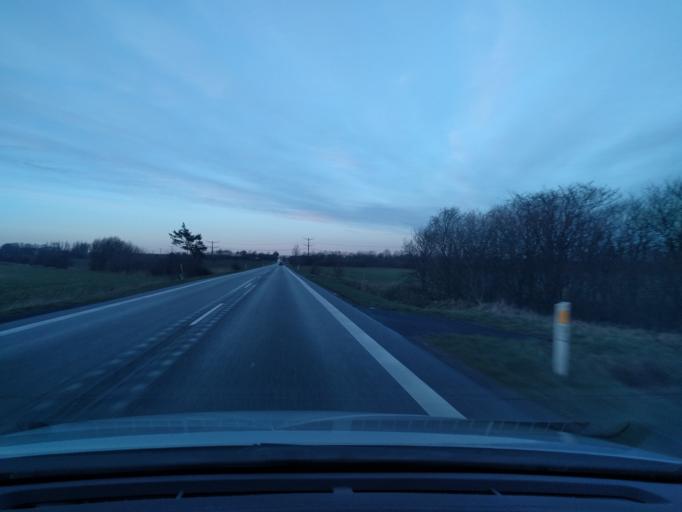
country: DK
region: South Denmark
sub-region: Tonder Kommune
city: Toftlund
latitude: 55.2429
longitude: 9.1330
